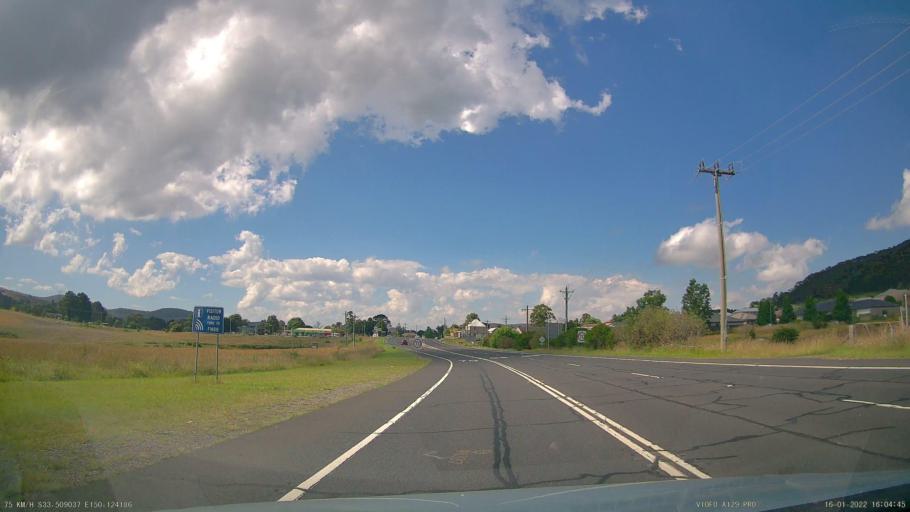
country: AU
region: New South Wales
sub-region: Lithgow
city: Bowenfels
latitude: -33.5086
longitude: 150.1243
